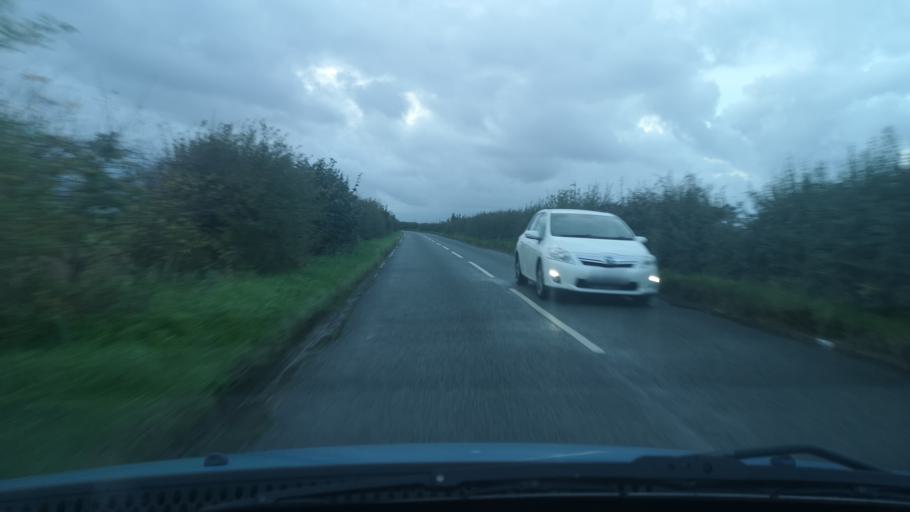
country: GB
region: England
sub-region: Doncaster
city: Norton
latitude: 53.6323
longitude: -1.1936
